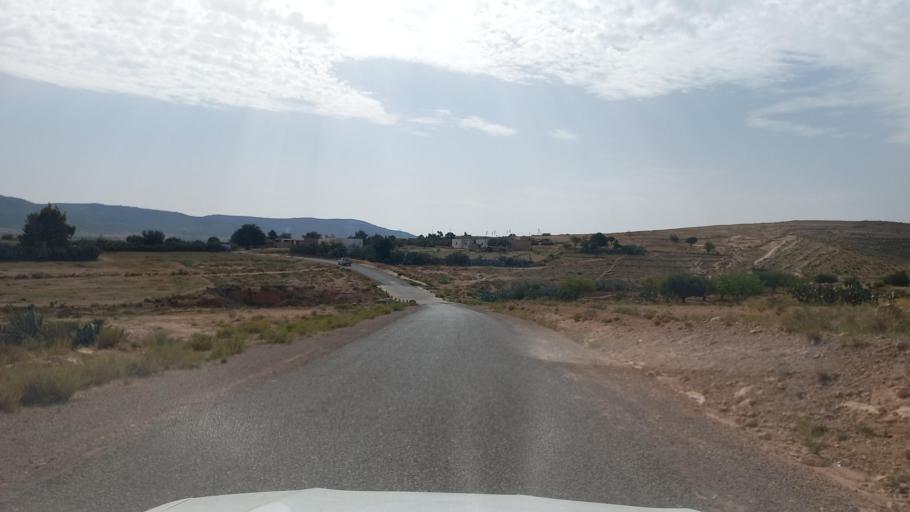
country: TN
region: Al Qasrayn
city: Kasserine
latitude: 35.3662
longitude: 8.8558
